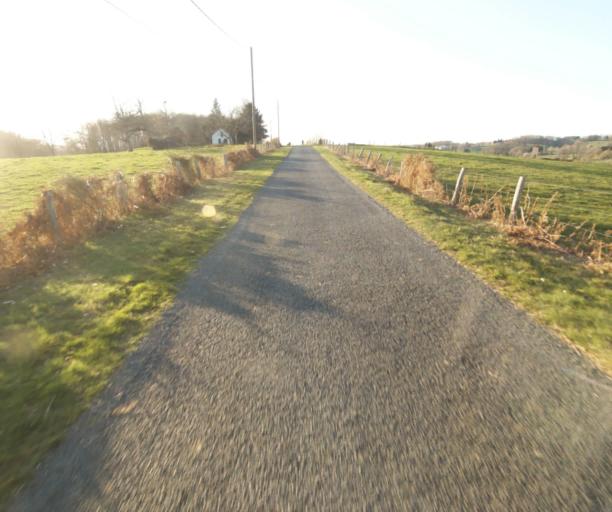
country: FR
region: Limousin
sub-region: Departement de la Correze
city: Uzerche
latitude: 45.3726
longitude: 1.5947
